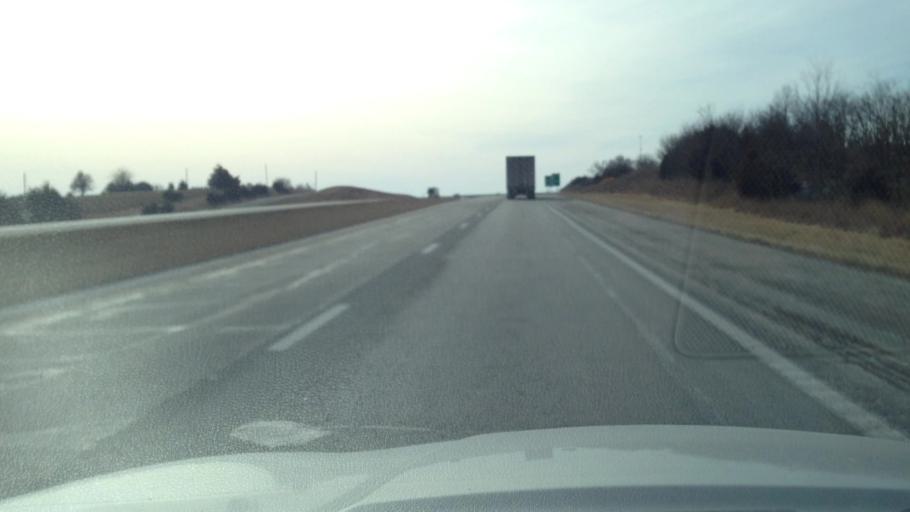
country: US
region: Missouri
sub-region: Harrison County
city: Bethany
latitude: 40.3820
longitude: -94.0010
